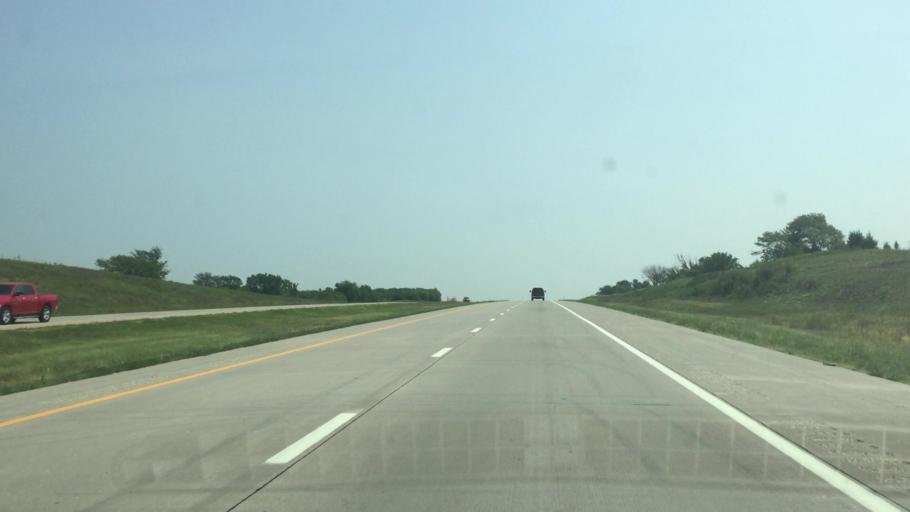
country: US
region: Kansas
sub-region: Osage County
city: Lyndon
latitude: 38.4385
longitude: -95.6905
